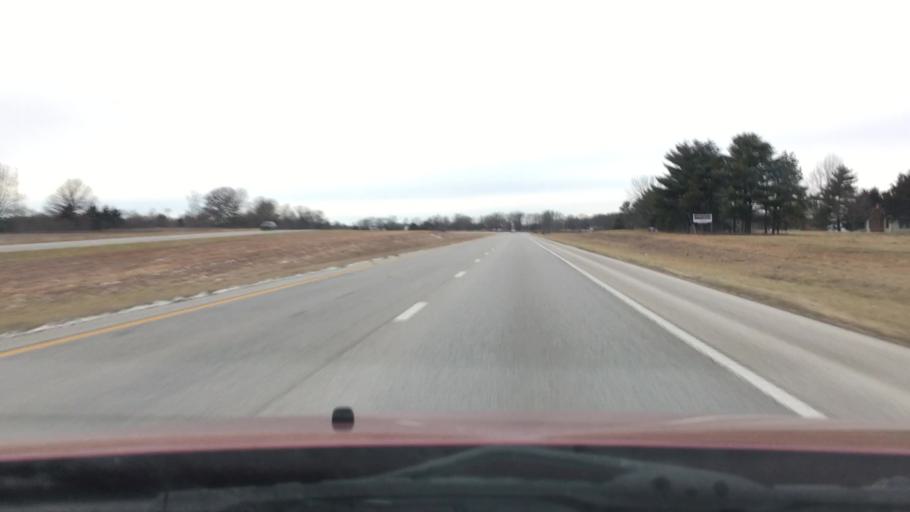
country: US
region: Missouri
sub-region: Webster County
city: Seymour
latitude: 37.1653
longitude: -92.8006
